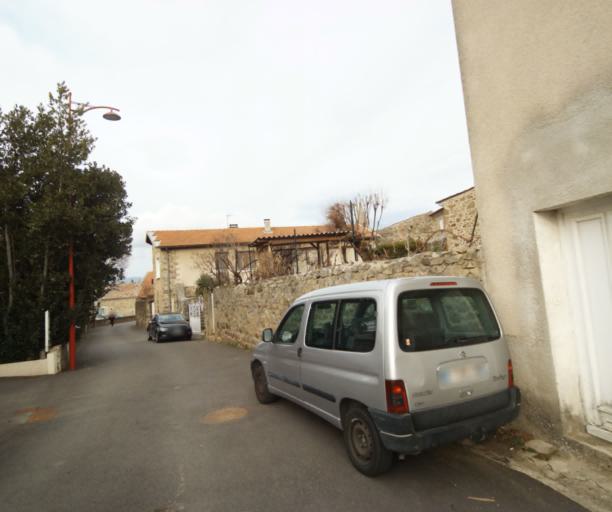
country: FR
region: Rhone-Alpes
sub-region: Departement de l'Ardeche
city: Davezieux
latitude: 45.2544
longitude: 4.7079
